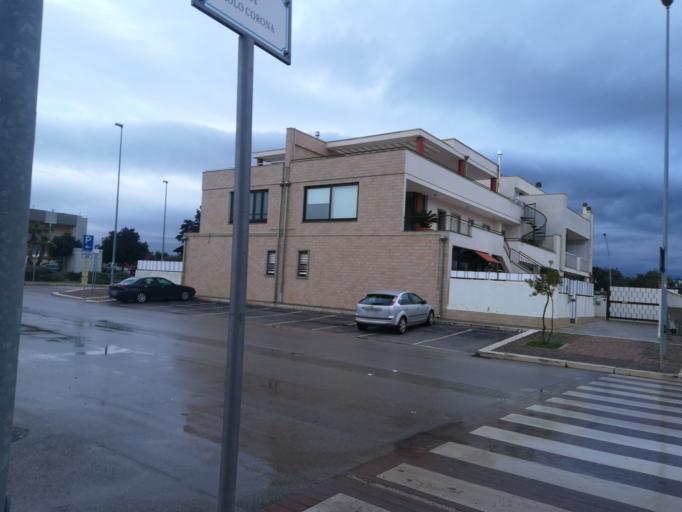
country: IT
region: Apulia
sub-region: Provincia di Bari
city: Polignano a Mare
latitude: 40.9930
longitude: 17.2132
